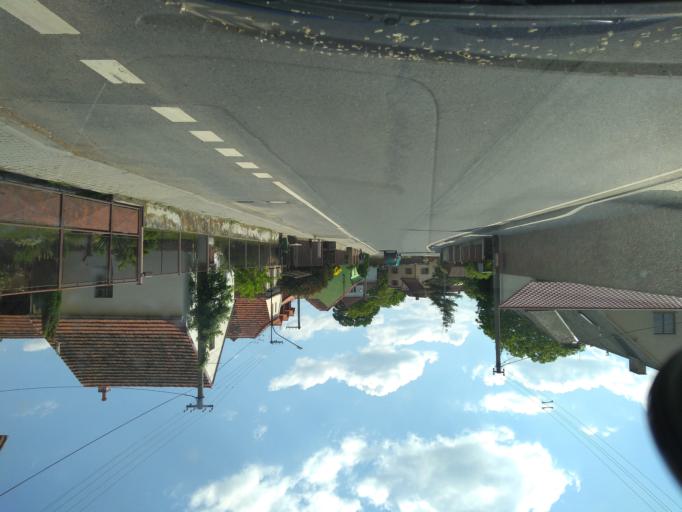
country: CZ
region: Plzensky
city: Prestice
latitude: 49.5605
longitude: 13.2984
